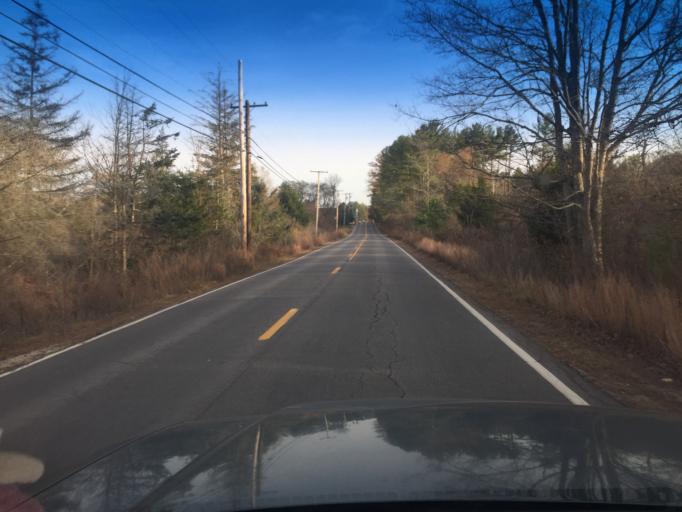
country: US
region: Maine
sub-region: York County
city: Eliot
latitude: 43.1830
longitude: -70.7395
